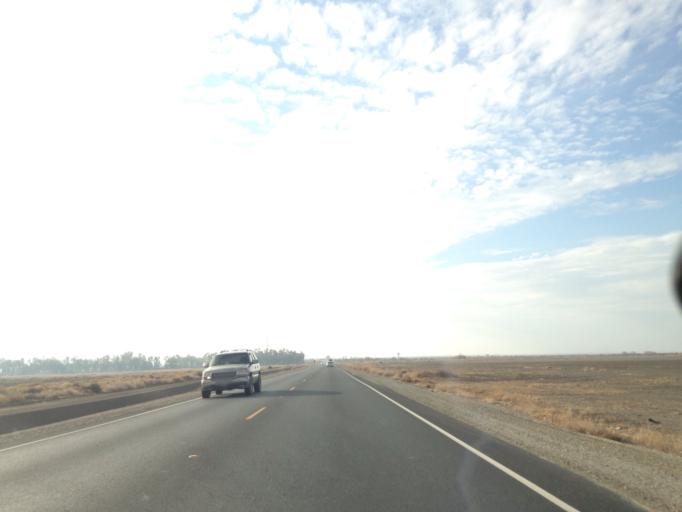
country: US
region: California
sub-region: Kern County
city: Lost Hills
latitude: 35.6162
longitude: -119.6362
